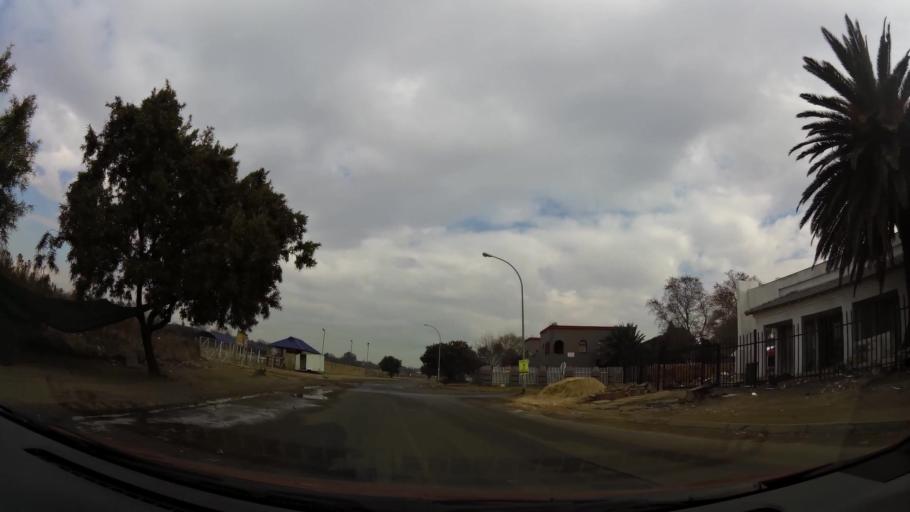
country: ZA
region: Gauteng
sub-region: Sedibeng District Municipality
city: Vanderbijlpark
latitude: -26.7123
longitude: 27.8606
